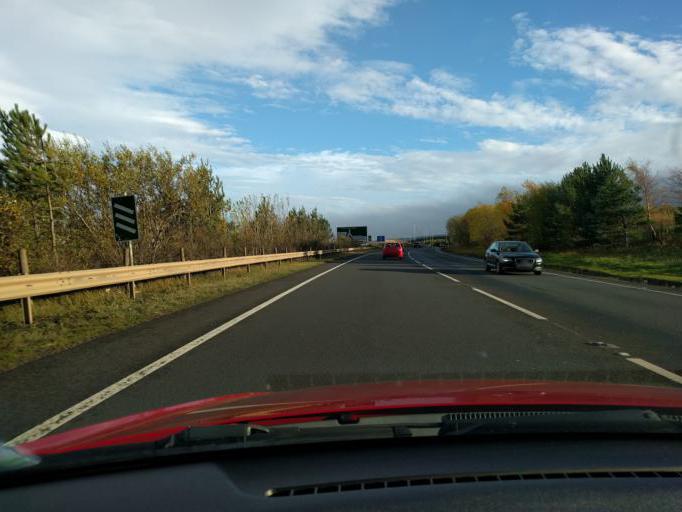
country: GB
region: Scotland
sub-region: East Lothian
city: Dunbar
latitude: 55.9418
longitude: -2.3656
